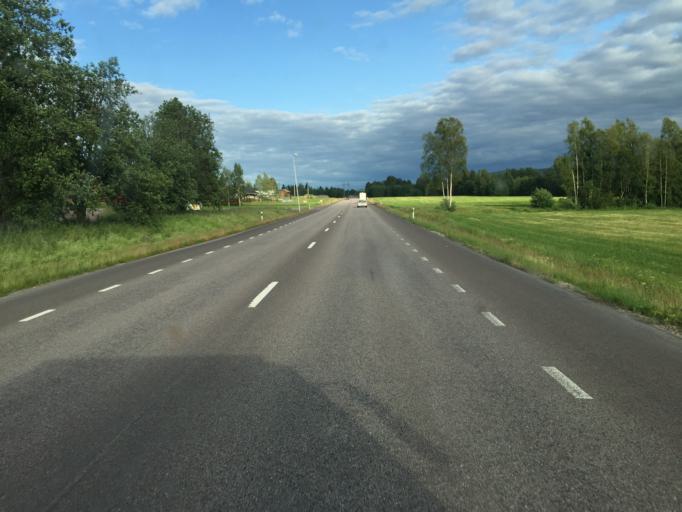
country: SE
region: Dalarna
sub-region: Gagnefs Kommun
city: Djuras
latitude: 60.5552
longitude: 15.1487
